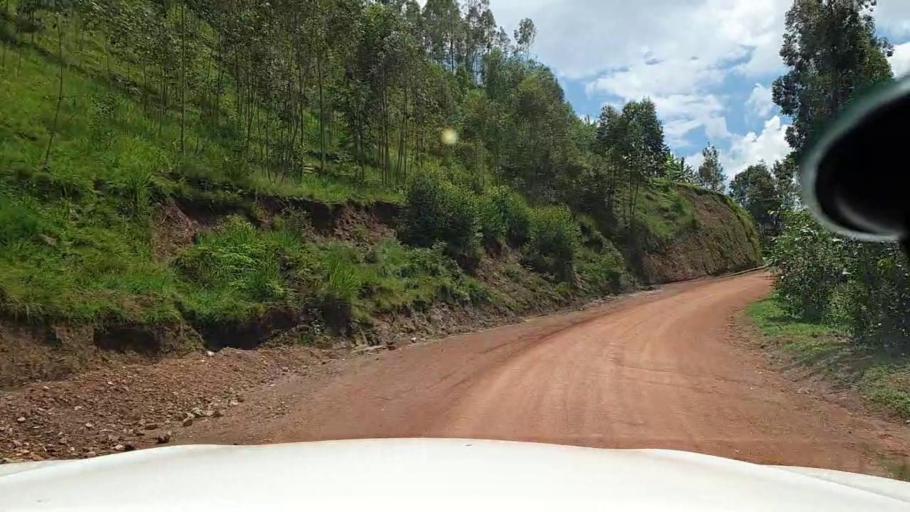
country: RW
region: Northern Province
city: Byumba
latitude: -1.7493
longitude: 29.8504
